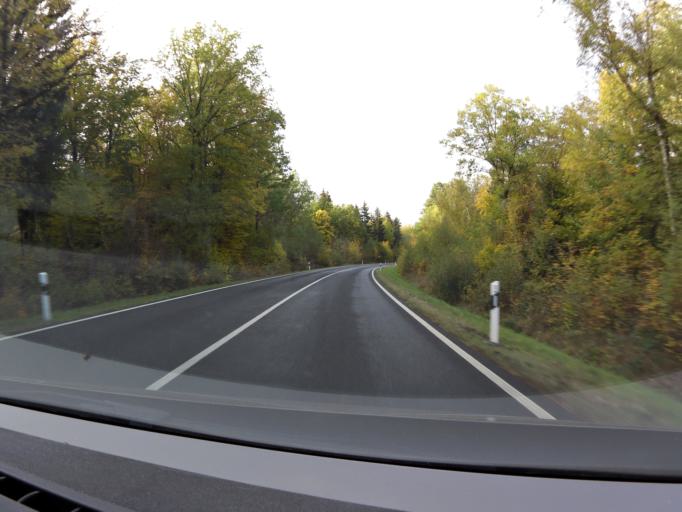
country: DE
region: Thuringia
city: Luisenthal
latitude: 50.7926
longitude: 10.7520
